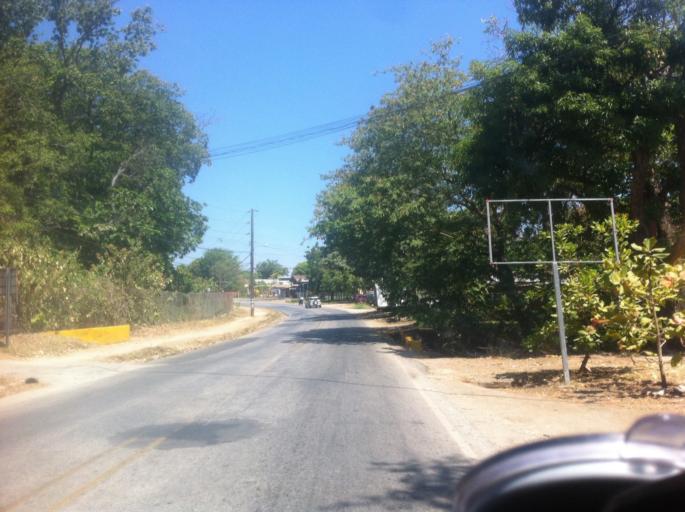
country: CR
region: Guanacaste
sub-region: Canton de Nicoya
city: Nicoya
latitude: 10.1294
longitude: -85.4417
